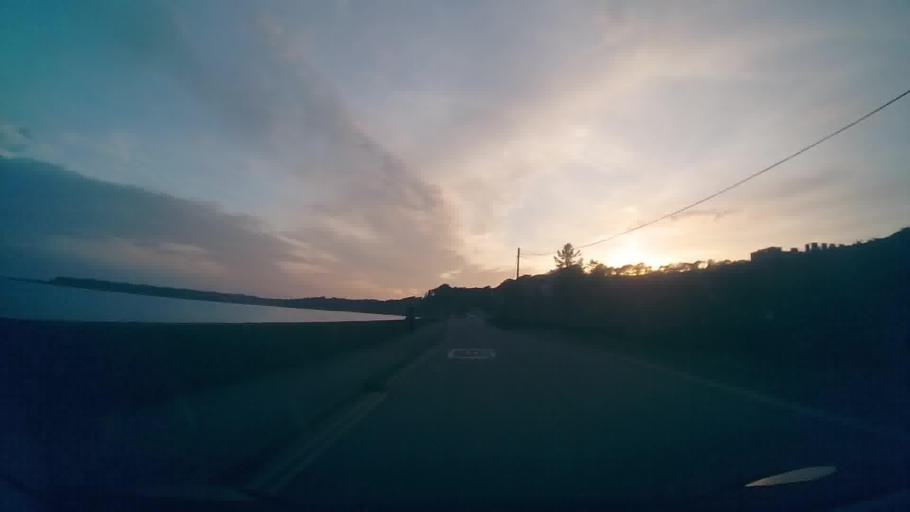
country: GB
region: Wales
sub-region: Pembrokeshire
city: Saundersfoot
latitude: 51.7335
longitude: -4.6510
